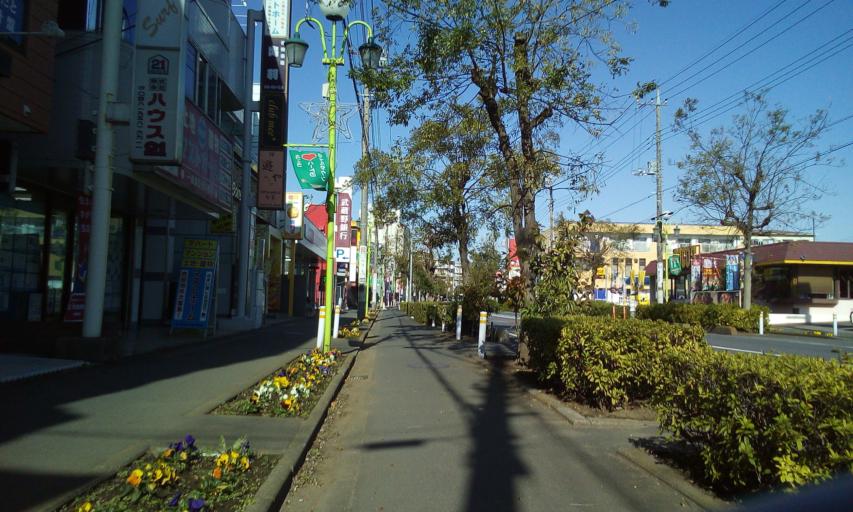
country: JP
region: Chiba
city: Nagareyama
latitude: 35.8484
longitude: 139.8848
